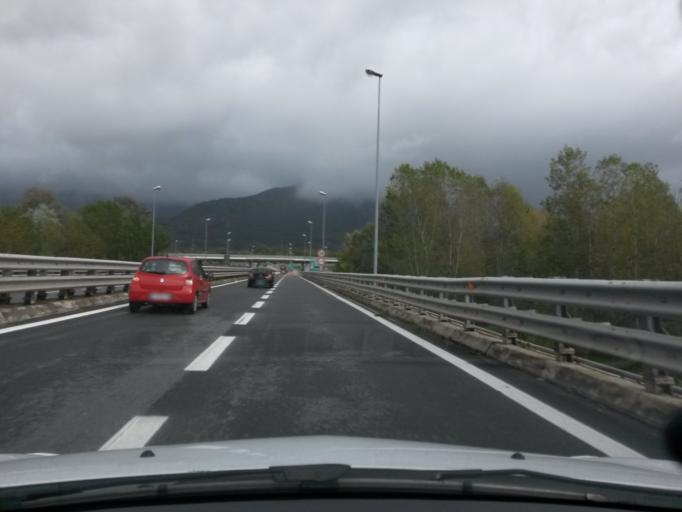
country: IT
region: Piedmont
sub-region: Provincia di Torino
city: Drubiaglio-Grangia
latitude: 45.0892
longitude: 7.4156
